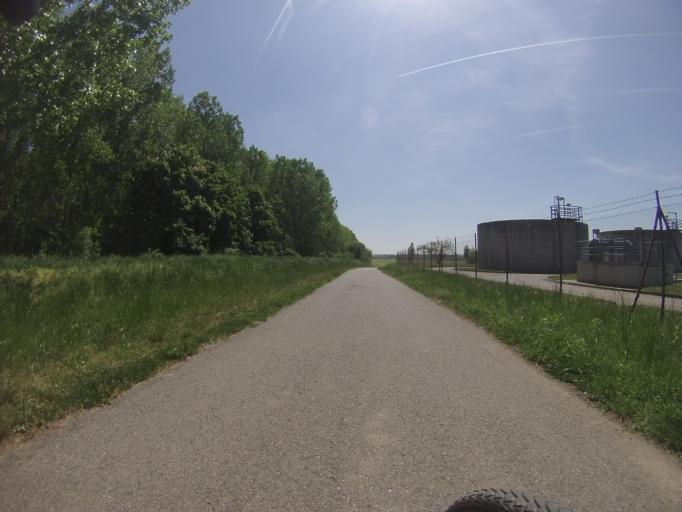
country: CZ
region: South Moravian
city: Zidlochovice
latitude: 49.0245
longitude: 16.6240
